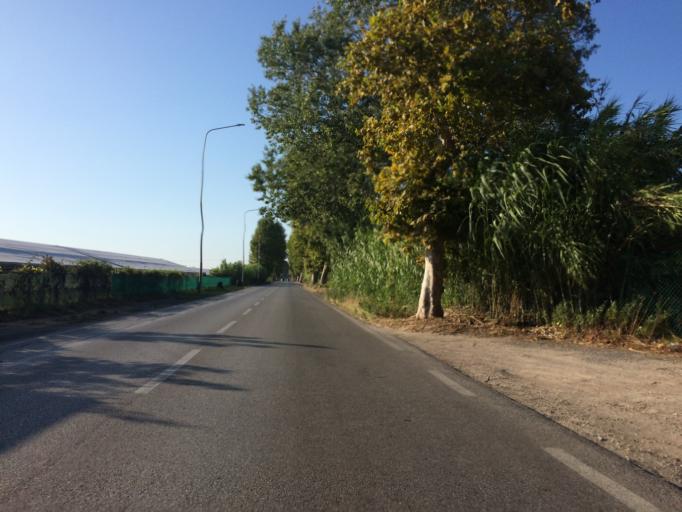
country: IT
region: Tuscany
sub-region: Provincia di Lucca
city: Torre del Lago Puccini
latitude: 43.8407
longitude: 10.2836
